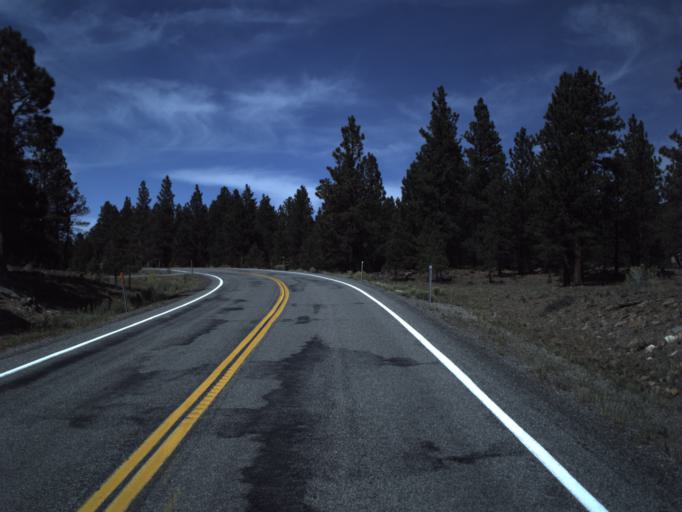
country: US
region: Utah
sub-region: Wayne County
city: Loa
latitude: 38.1657
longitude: -111.3369
